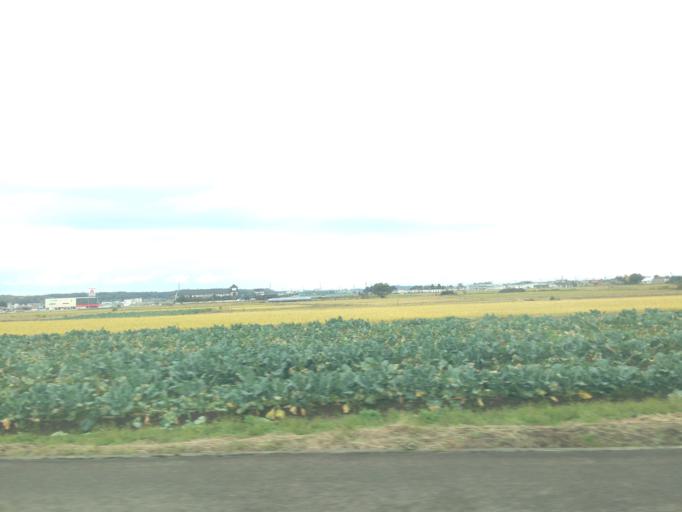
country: JP
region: Ishikawa
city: Komatsu
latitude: 36.3002
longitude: 136.3643
